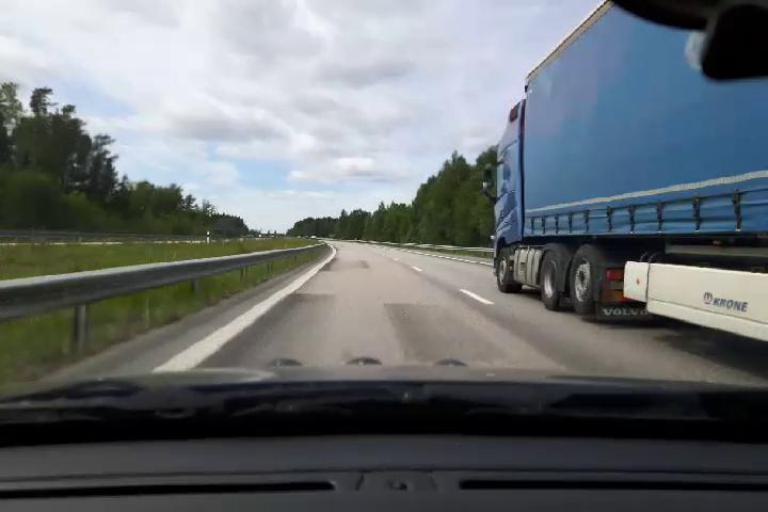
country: SE
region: Uppsala
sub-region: Alvkarleby Kommun
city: AElvkarleby
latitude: 60.4693
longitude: 17.4024
